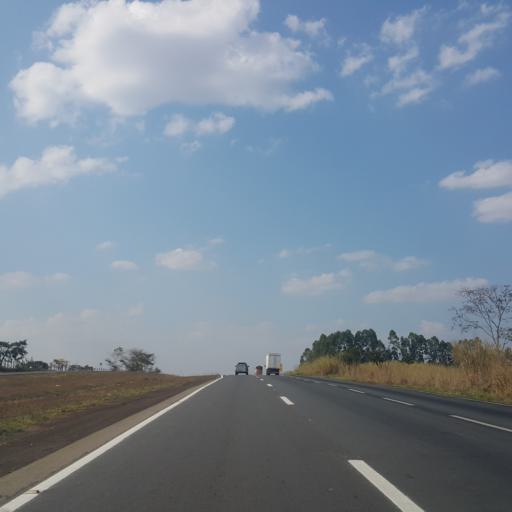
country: BR
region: Goias
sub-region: Abadiania
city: Abadiania
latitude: -16.2864
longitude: -48.7972
